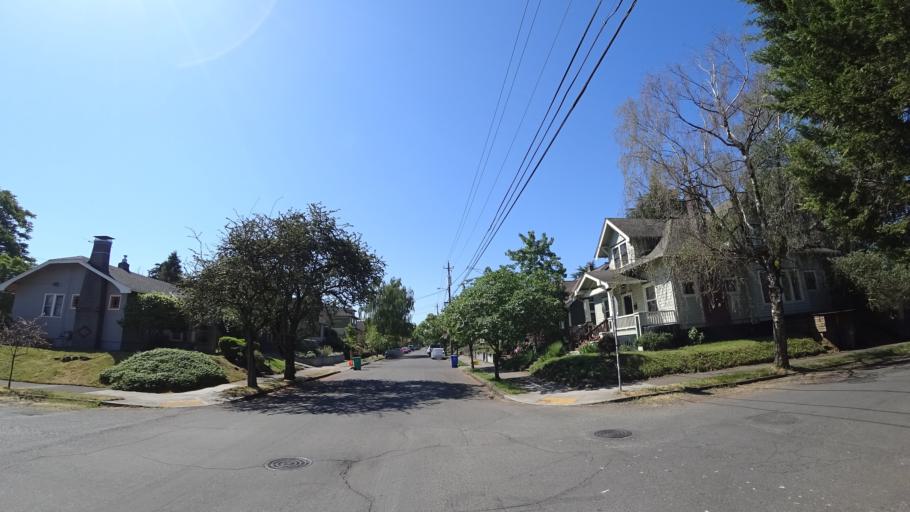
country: US
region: Oregon
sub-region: Multnomah County
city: Portland
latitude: 45.5617
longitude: -122.6468
